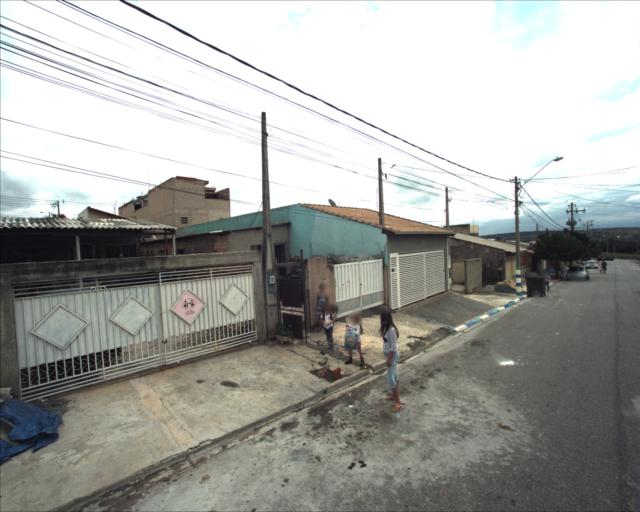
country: BR
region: Sao Paulo
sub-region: Sorocaba
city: Sorocaba
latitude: -23.4232
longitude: -47.4650
